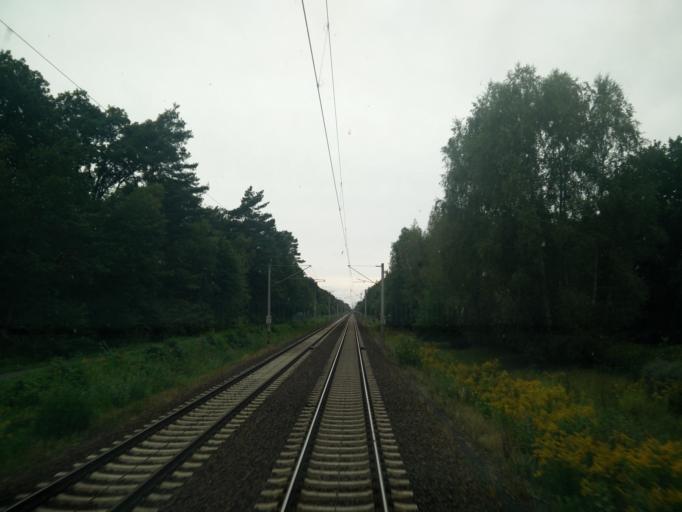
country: DE
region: Brandenburg
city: Dallgow-Doeberitz
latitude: 52.5723
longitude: 13.0411
